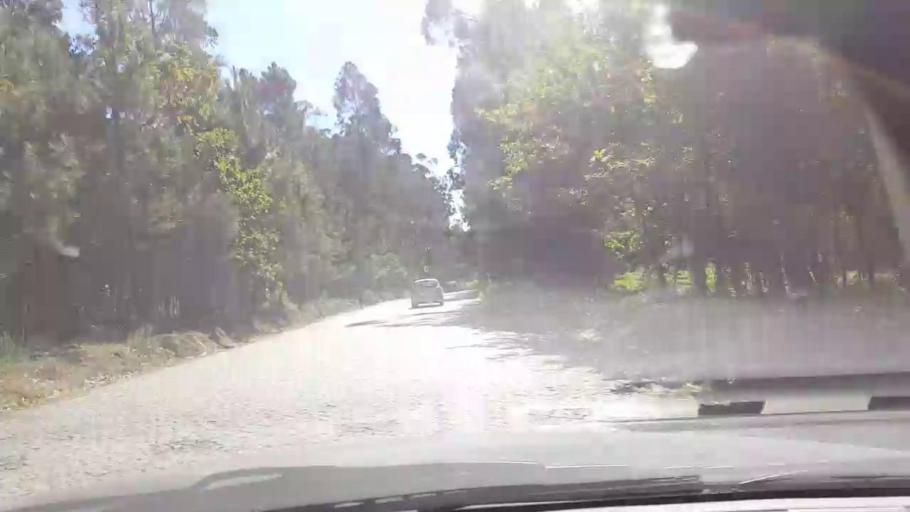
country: PT
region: Porto
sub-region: Vila do Conde
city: Arvore
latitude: 41.3233
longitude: -8.7249
